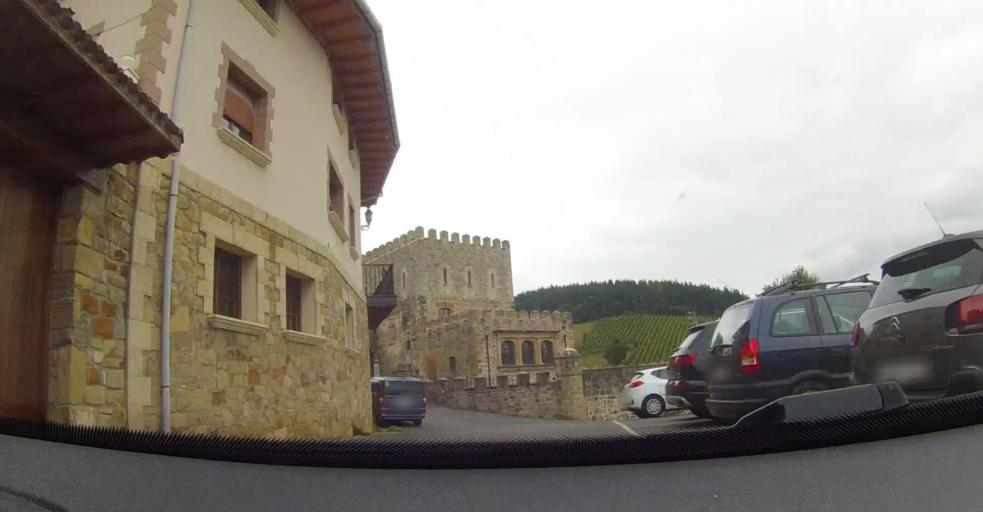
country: ES
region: Basque Country
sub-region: Bizkaia
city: Urrestieta
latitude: 43.2292
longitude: -3.1623
